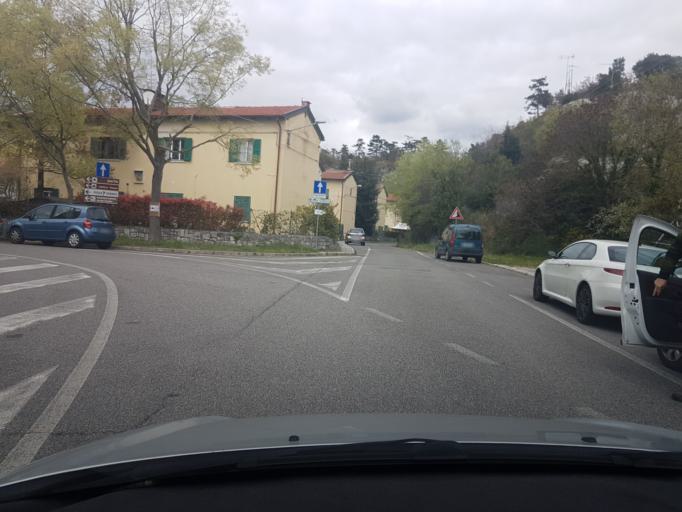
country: IT
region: Friuli Venezia Giulia
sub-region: Provincia di Trieste
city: Duino
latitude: 45.7819
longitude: 13.5874
